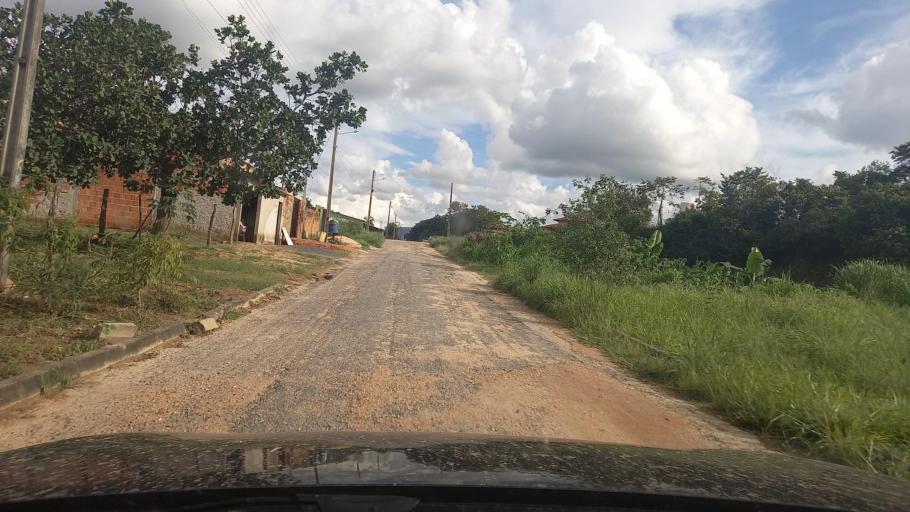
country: BR
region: Goias
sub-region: Cavalcante
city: Cavalcante
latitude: -13.7993
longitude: -47.4468
